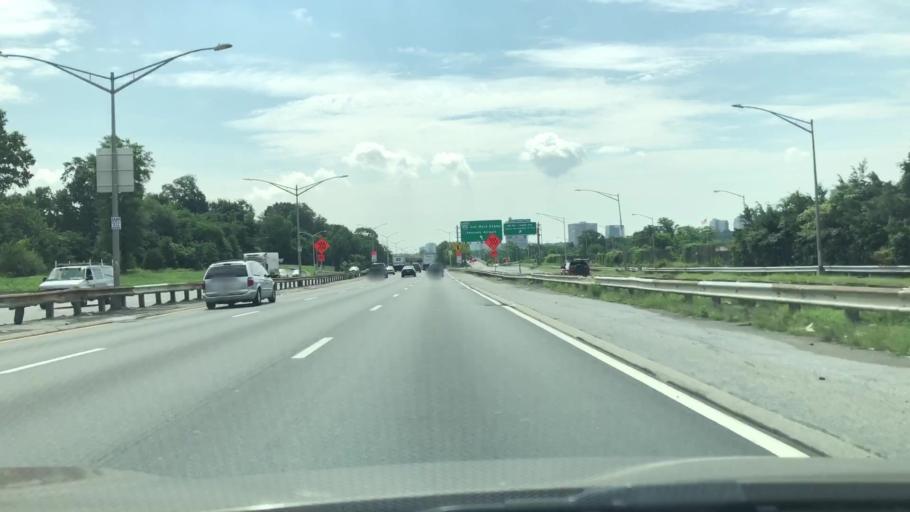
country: US
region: New York
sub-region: Queens County
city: Jamaica
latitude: 40.7322
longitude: -73.8352
